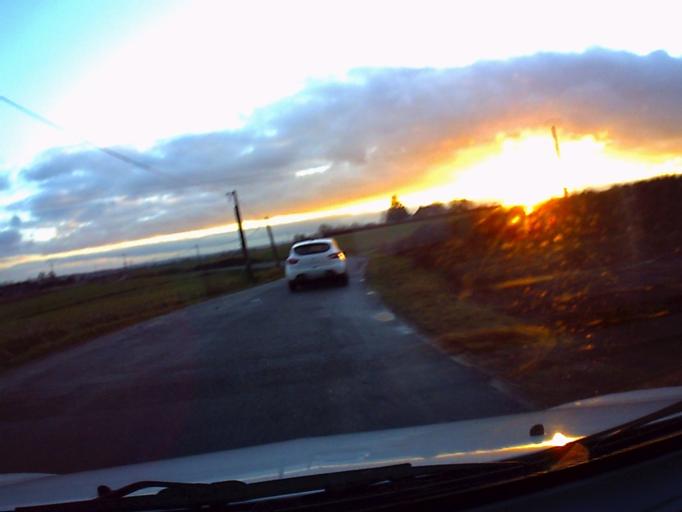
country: FR
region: Brittany
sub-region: Departement d'Ille-et-Vilaine
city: Iffendic
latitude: 48.1470
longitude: -2.0155
